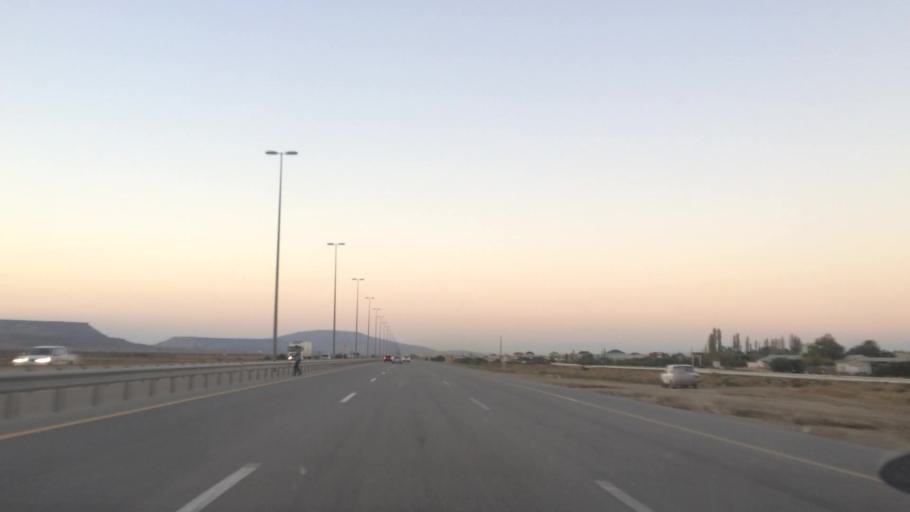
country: AZ
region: Baki
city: Qobustan
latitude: 40.0219
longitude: 49.4248
